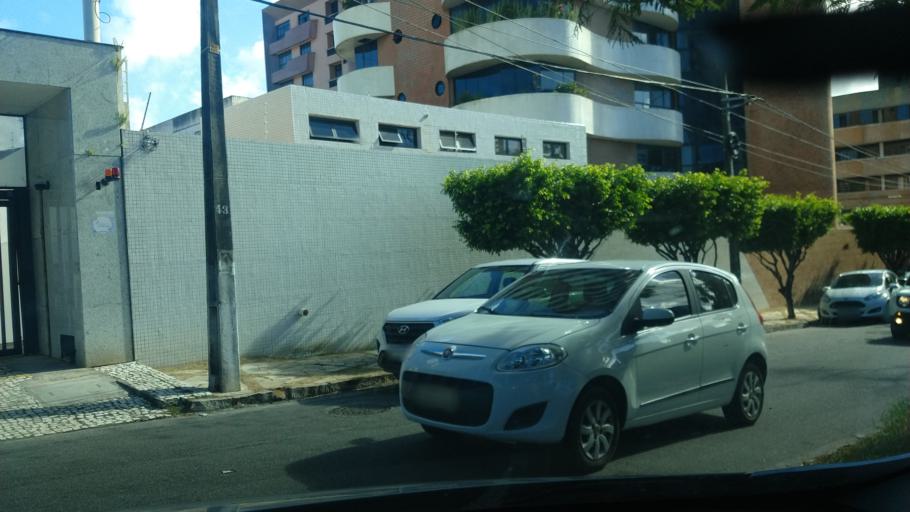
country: BR
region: Rio Grande do Norte
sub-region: Natal
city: Natal
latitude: -5.8311
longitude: -35.2190
